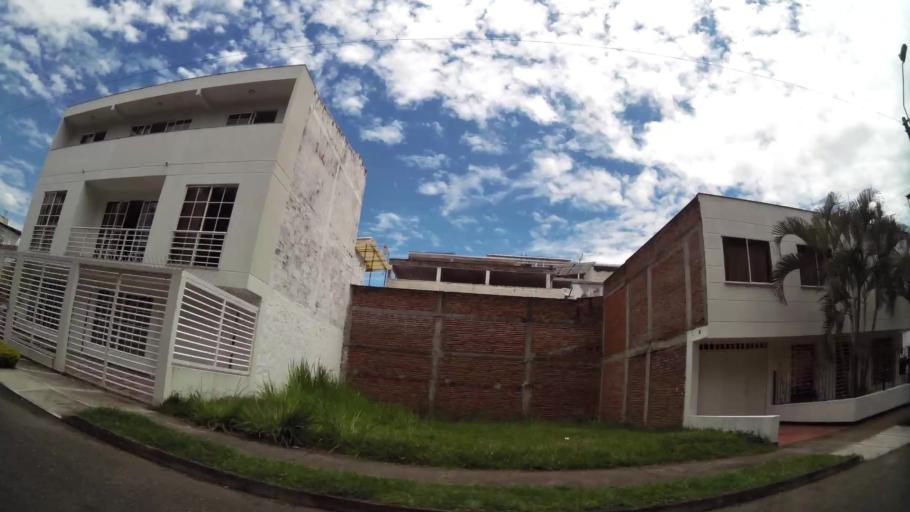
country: CO
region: Valle del Cauca
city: Cali
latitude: 3.3842
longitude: -76.5276
